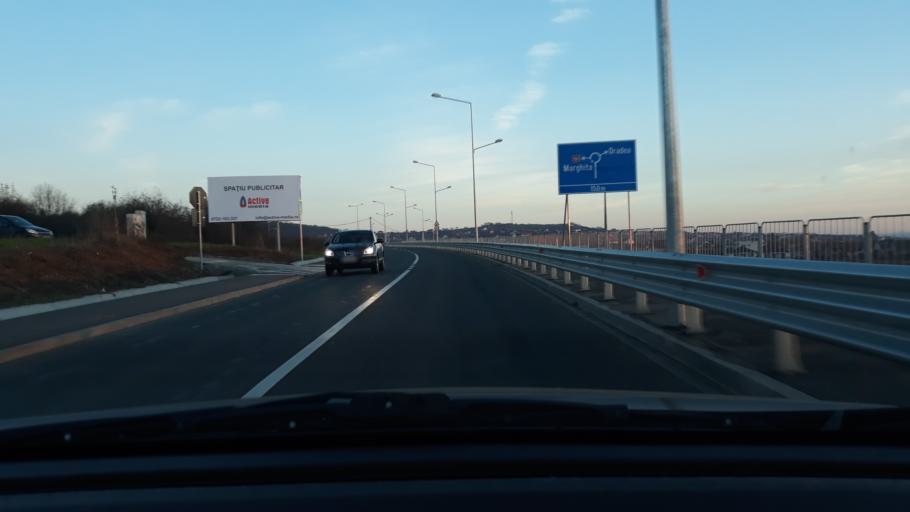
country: RO
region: Bihor
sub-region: Comuna Biharea
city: Oradea
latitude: 47.0977
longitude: 21.9211
